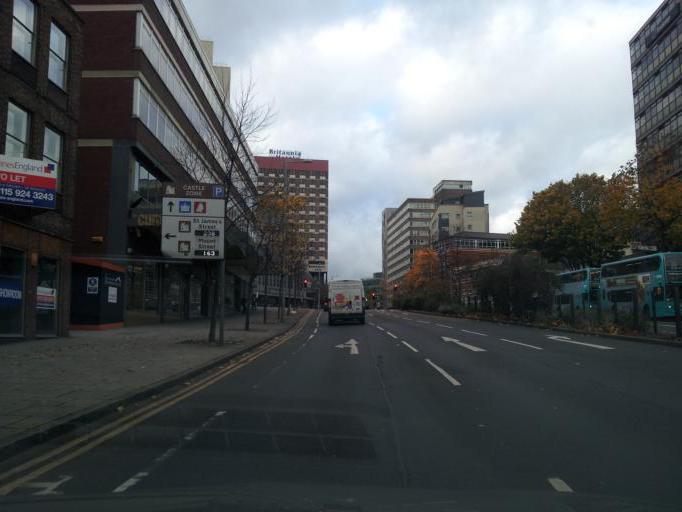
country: GB
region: England
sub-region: Nottingham
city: Nottingham
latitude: 52.9510
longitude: -1.1520
